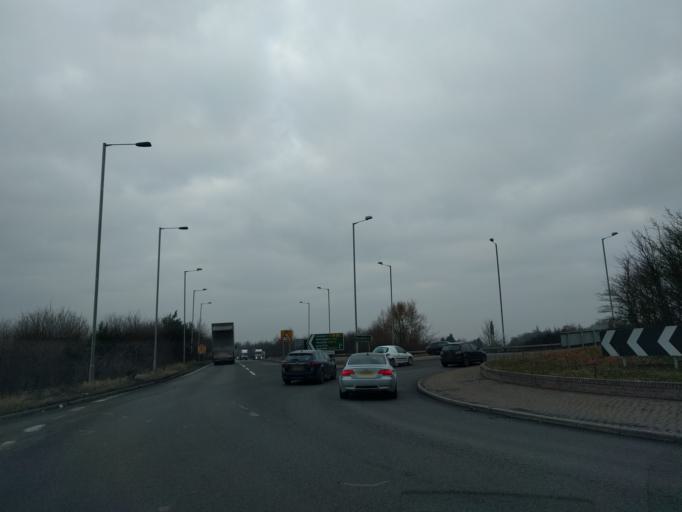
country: GB
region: England
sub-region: Nottinghamshire
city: Newark on Trent
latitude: 53.0927
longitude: -0.7891
